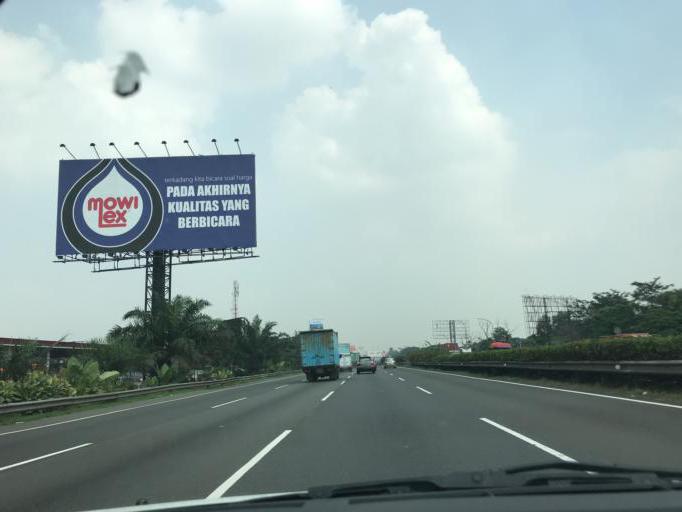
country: ID
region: West Java
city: Ciputat
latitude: -6.2138
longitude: 106.6823
